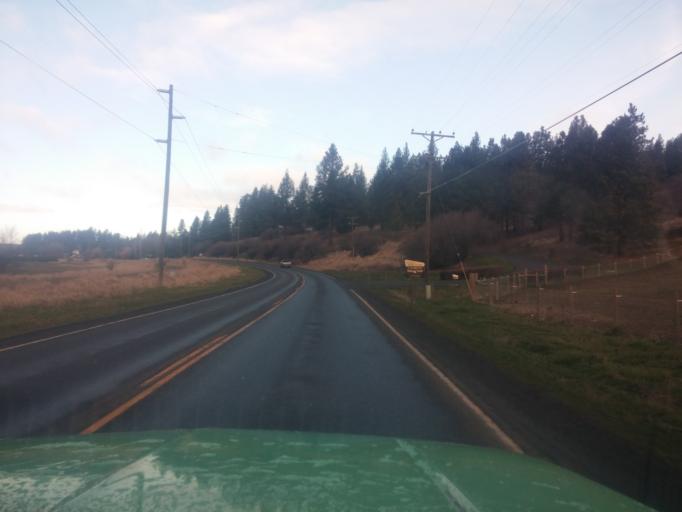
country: US
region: Idaho
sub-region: Latah County
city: Moscow
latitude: 46.9286
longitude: -116.9078
